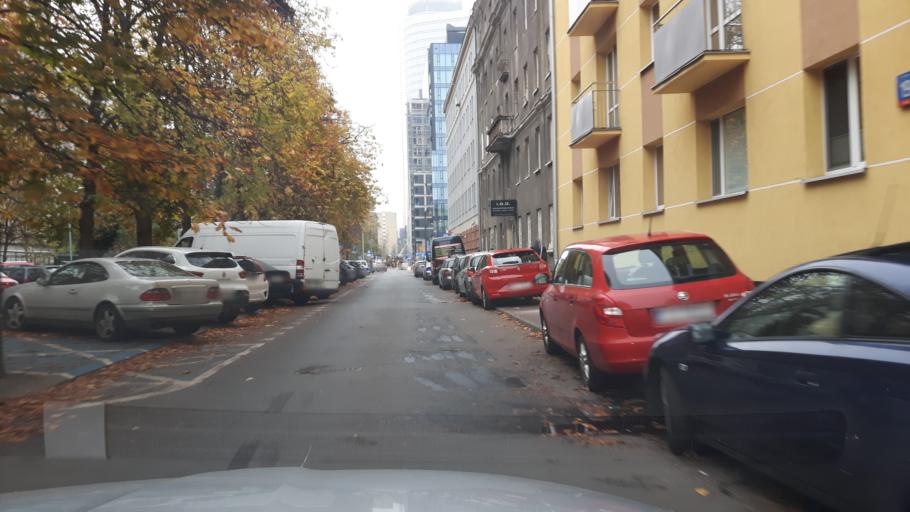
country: PL
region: Masovian Voivodeship
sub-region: Warszawa
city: Wola
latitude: 52.2363
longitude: 20.9918
